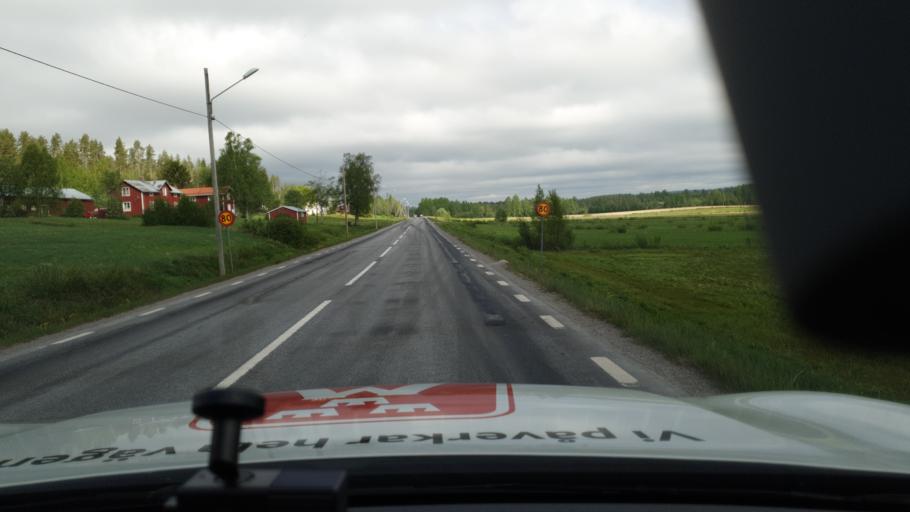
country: SE
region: Vaesterbotten
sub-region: Umea Kommun
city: Roback
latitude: 63.9185
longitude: 20.1934
